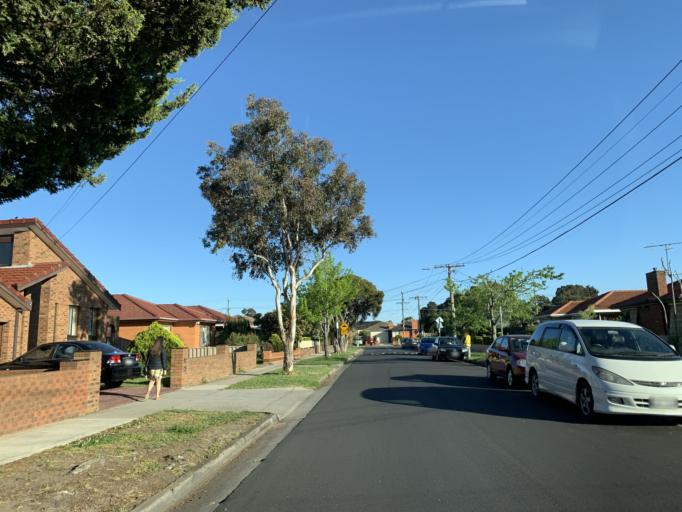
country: AU
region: Victoria
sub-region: Brimbank
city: St Albans
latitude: -37.7587
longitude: 144.8119
